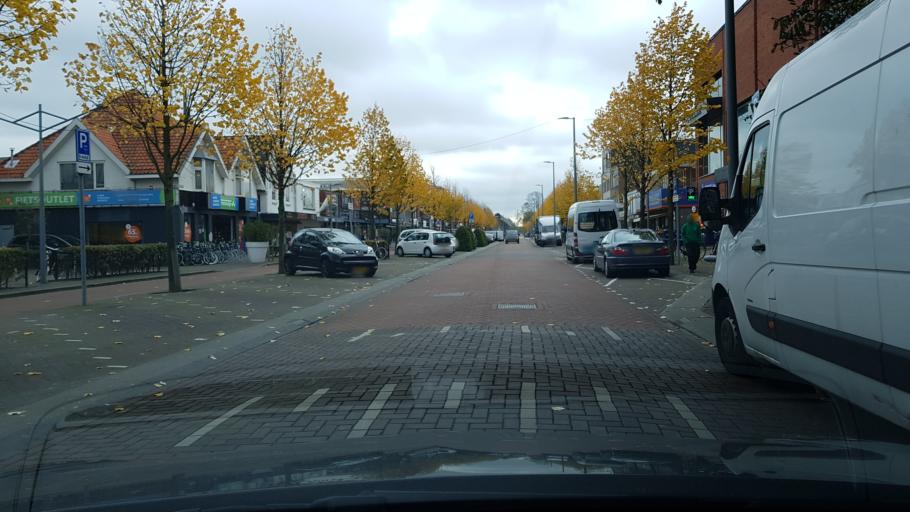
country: NL
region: North Holland
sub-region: Gemeente Haarlemmermeer
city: Hoofddorp
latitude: 52.3044
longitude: 4.6948
